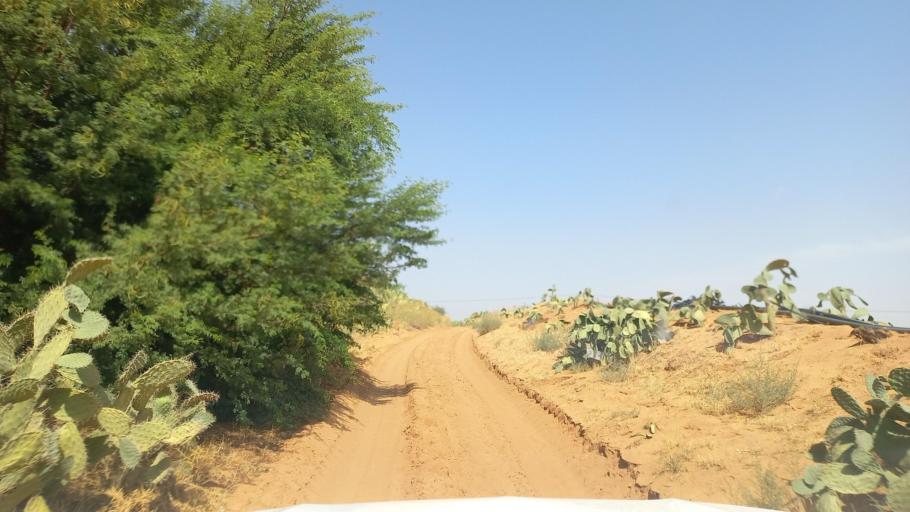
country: TN
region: Al Qasrayn
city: Kasserine
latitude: 35.2455
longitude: 9.0583
